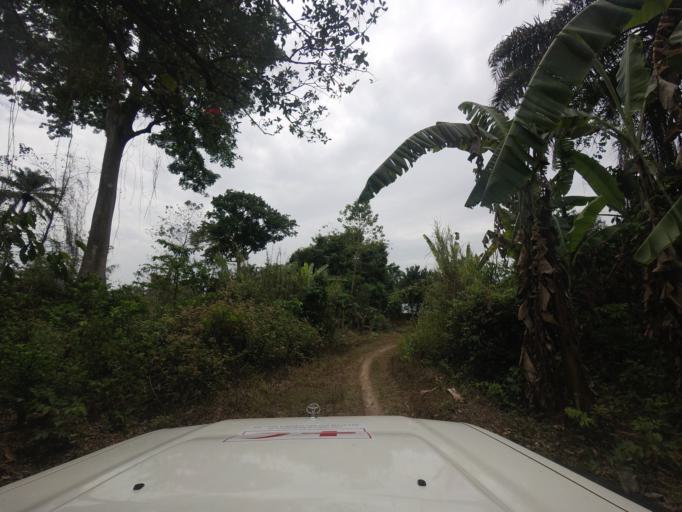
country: SL
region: Eastern Province
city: Buedu
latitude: 8.4293
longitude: -10.2686
